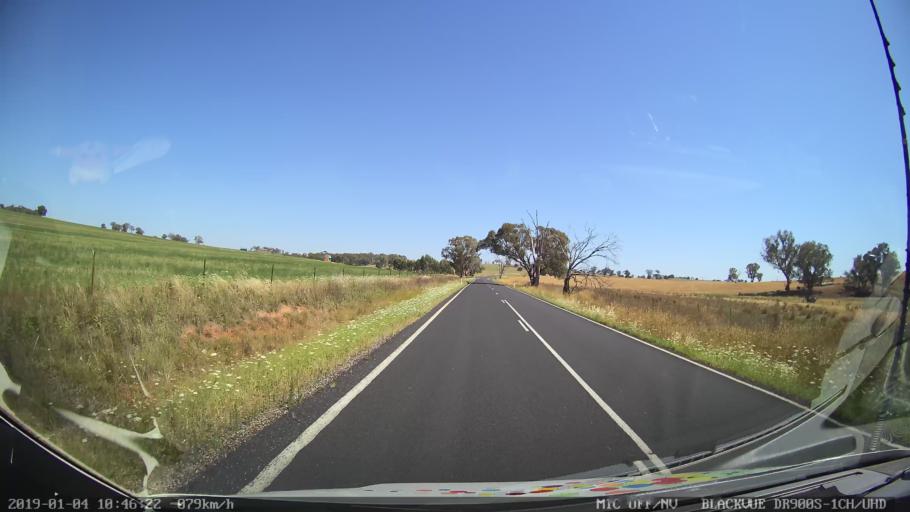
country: AU
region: New South Wales
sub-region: Cabonne
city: Molong
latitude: -33.2819
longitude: 148.7229
